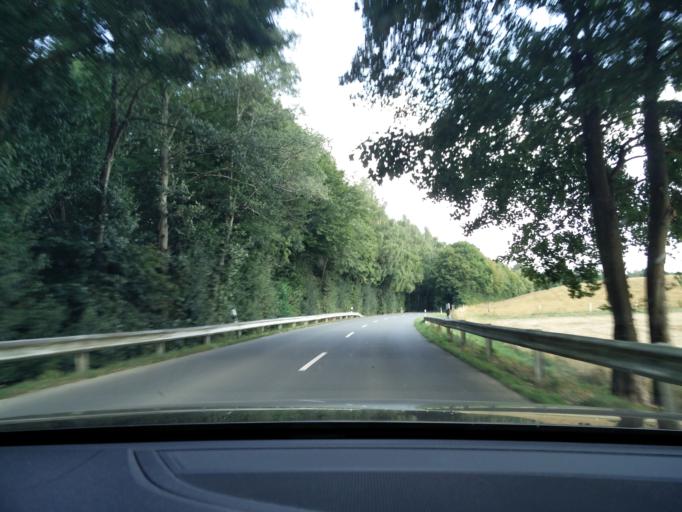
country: DE
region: North Rhine-Westphalia
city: Lichtenau
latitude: 51.6678
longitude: 8.9278
